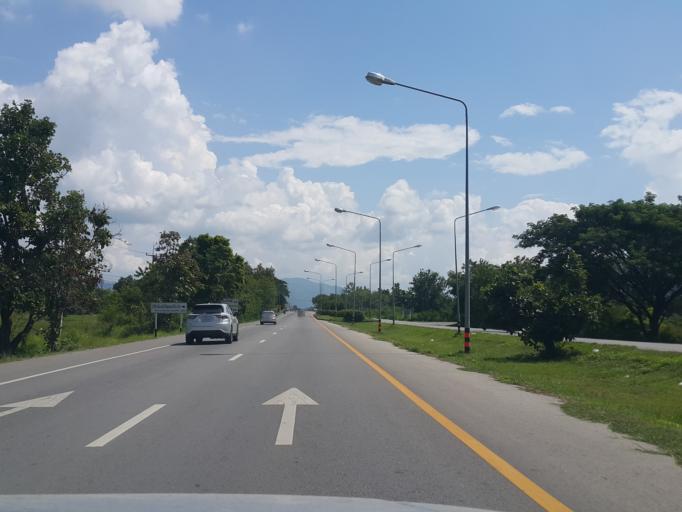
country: TH
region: Chiang Mai
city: San Kamphaeng
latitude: 18.7231
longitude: 99.1075
